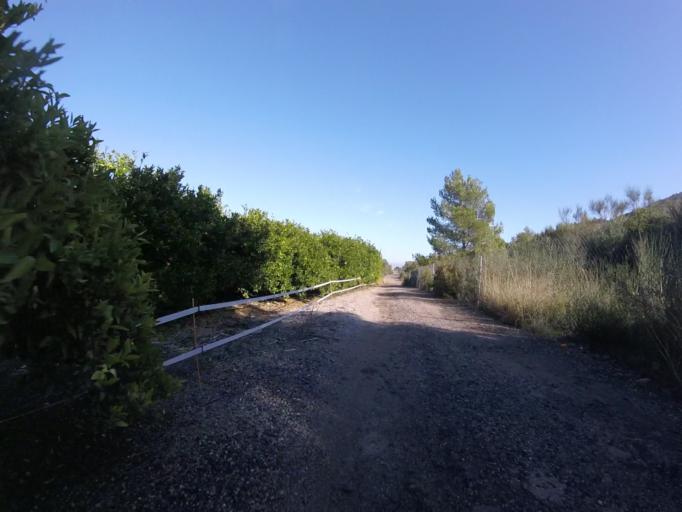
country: ES
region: Valencia
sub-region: Provincia de Castello
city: Santa Magdalena de Pulpis
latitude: 40.3794
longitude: 0.3400
